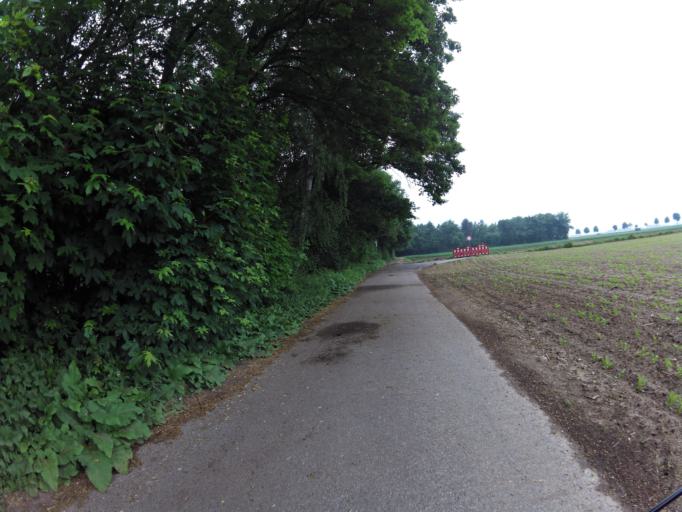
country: DE
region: North Rhine-Westphalia
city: Geilenkirchen
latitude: 50.9996
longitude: 6.1144
